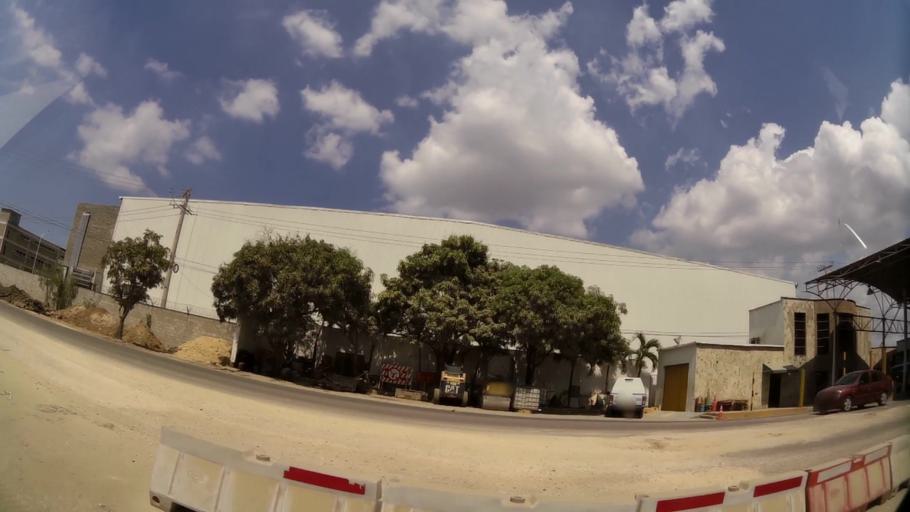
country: CO
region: Bolivar
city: Cartagena
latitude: 10.3424
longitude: -75.4910
